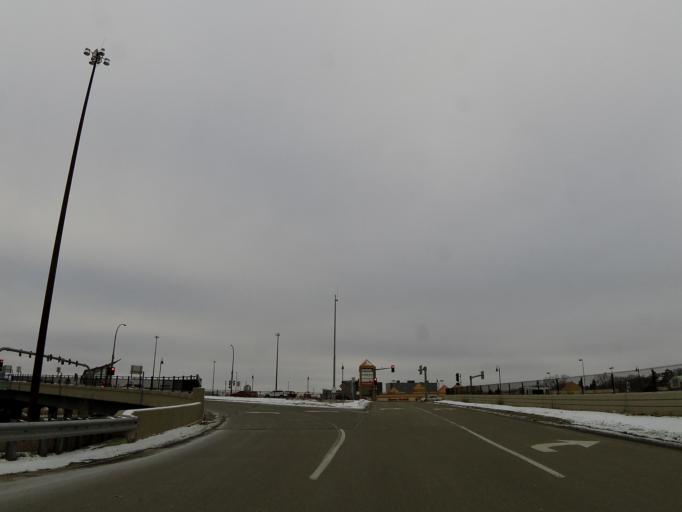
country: US
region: Minnesota
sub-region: Hennepin County
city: Richfield
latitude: 44.8624
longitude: -93.2871
